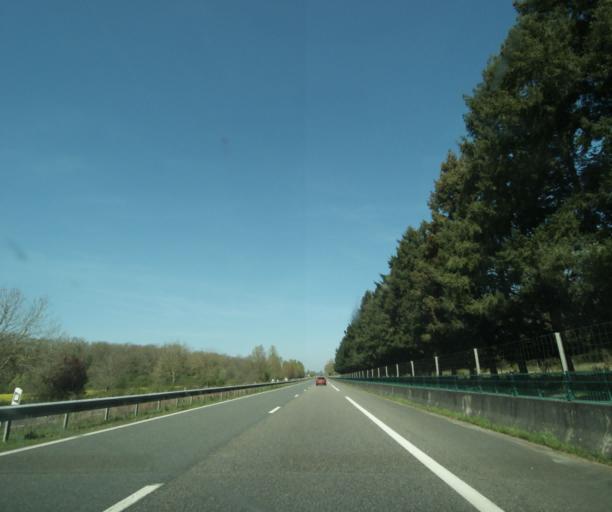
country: FR
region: Bourgogne
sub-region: Departement de la Nievre
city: La Charite-sur-Loire
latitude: 47.2097
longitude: 3.0084
